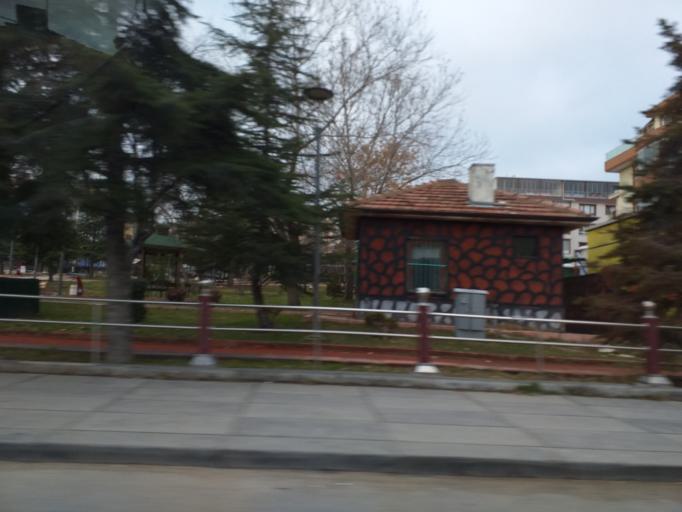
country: TR
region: Ankara
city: Ankara
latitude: 39.9787
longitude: 32.8203
